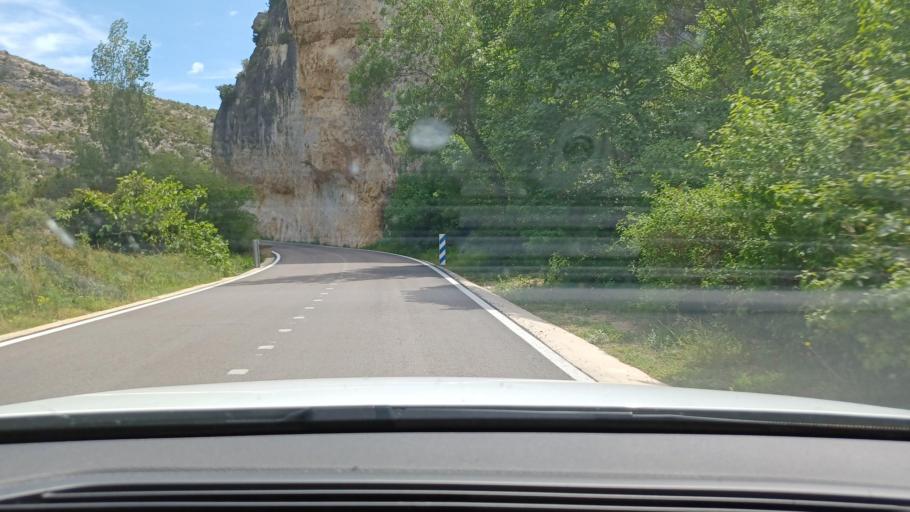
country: ES
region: Valencia
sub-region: Provincia de Castello
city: Rosell
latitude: 40.6611
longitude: 0.2658
